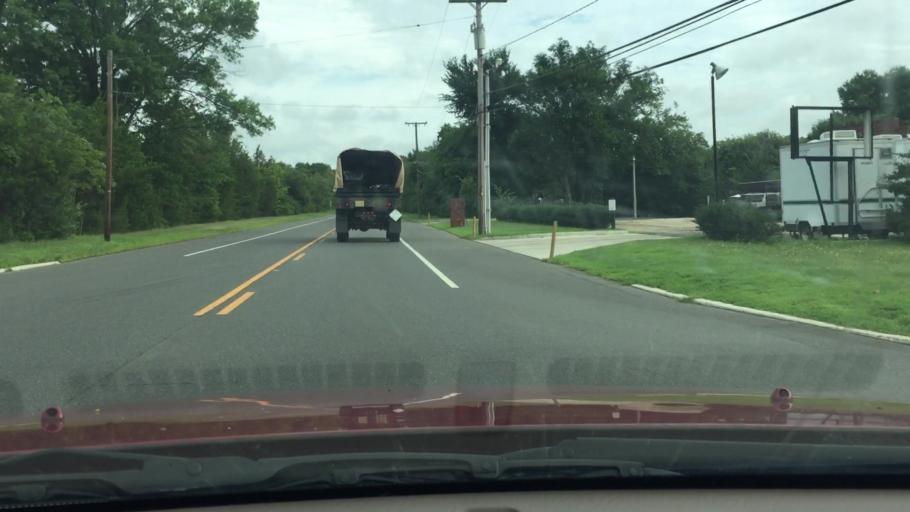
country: US
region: New Jersey
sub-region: Burlington County
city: Fort Dix
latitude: 40.0429
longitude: -74.6454
